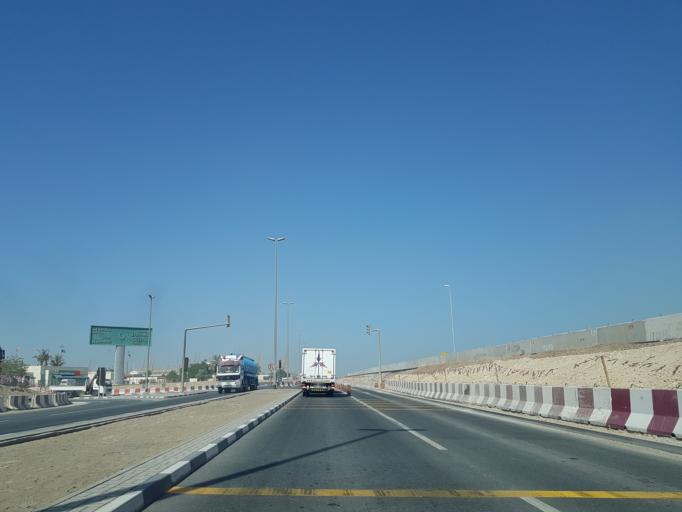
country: AE
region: Dubai
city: Dubai
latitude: 25.0152
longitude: 55.0893
